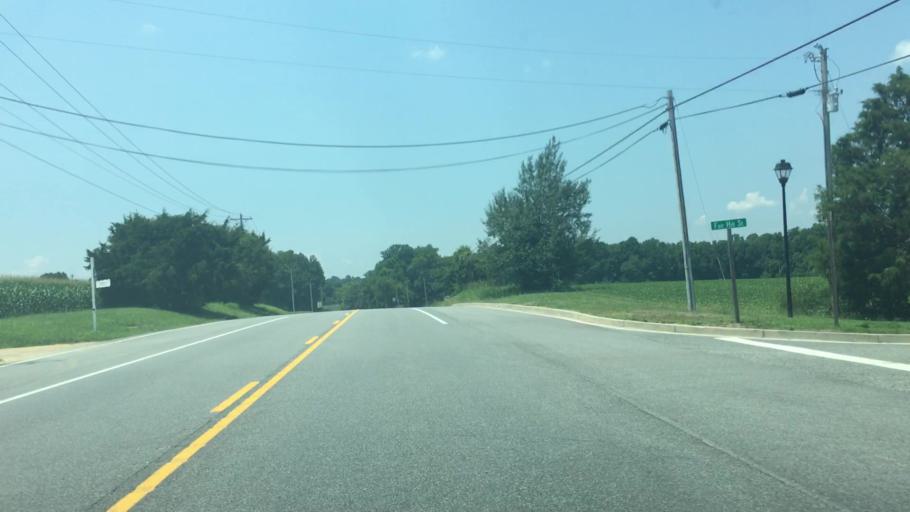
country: US
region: Maryland
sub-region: Saint Mary's County
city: Mechanicsville
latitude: 38.3772
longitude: -76.7012
